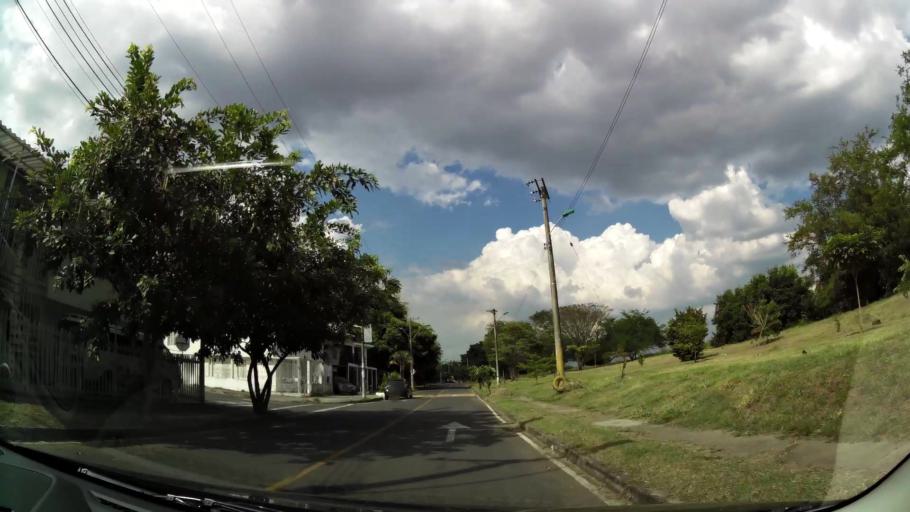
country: CO
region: Valle del Cauca
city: Cali
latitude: 3.3960
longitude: -76.5028
